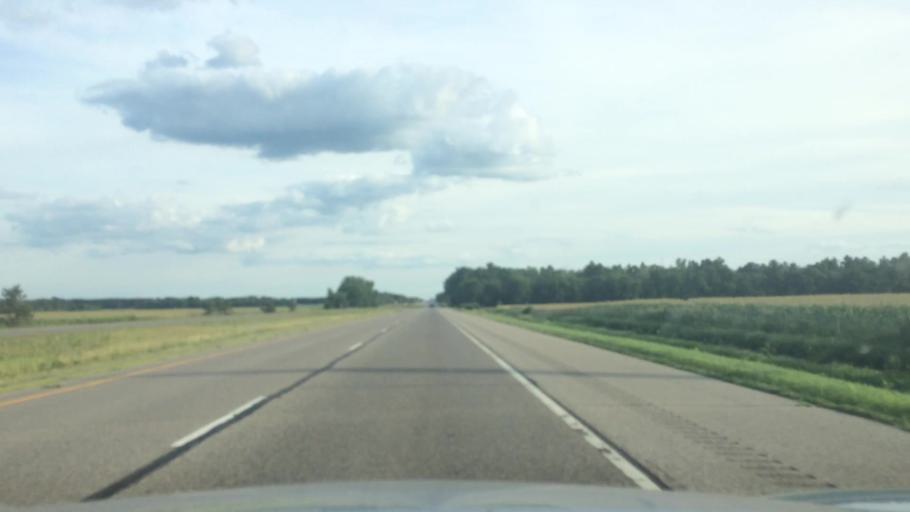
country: US
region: Wisconsin
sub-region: Portage County
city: Plover
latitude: 44.2781
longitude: -89.5238
